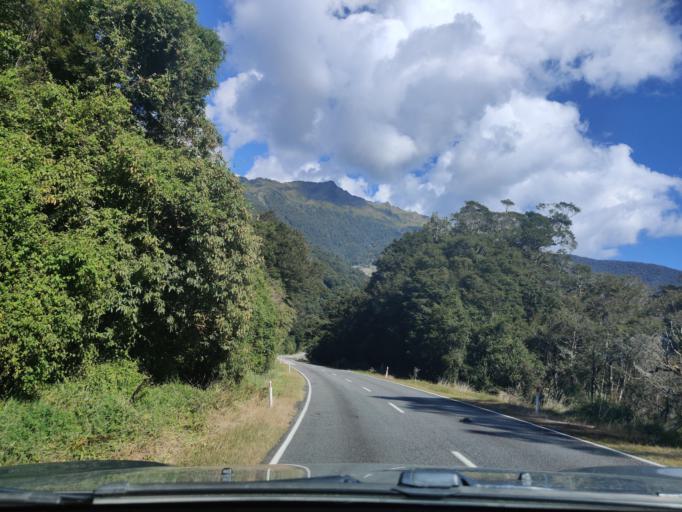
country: NZ
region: Otago
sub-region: Queenstown-Lakes District
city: Wanaka
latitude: -43.9712
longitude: 169.3942
